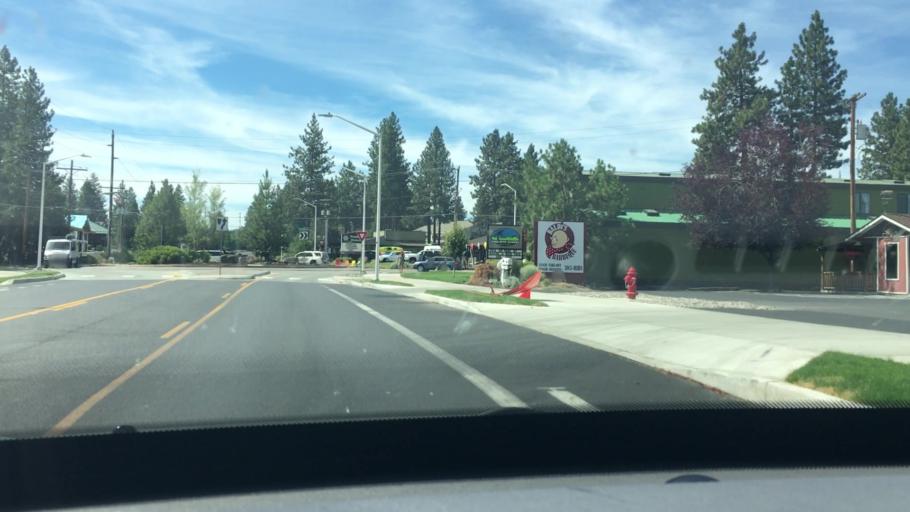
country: US
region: Oregon
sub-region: Deschutes County
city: Bend
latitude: 44.0486
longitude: -121.3318
